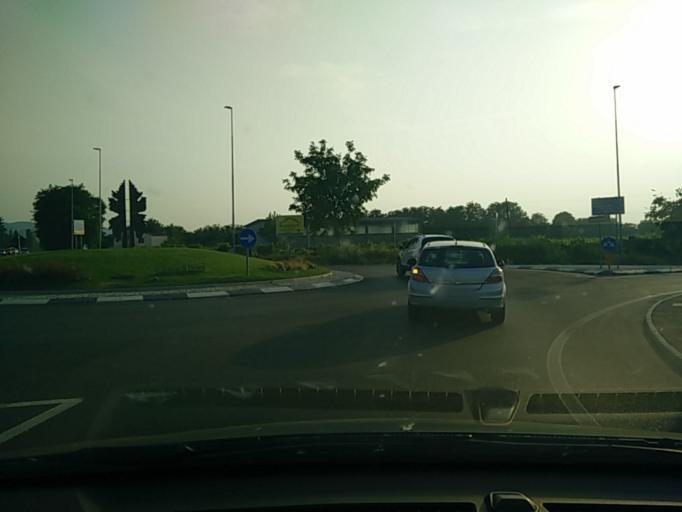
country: IT
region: Lombardy
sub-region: Provincia di Pavia
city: Broni
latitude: 45.0578
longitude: 9.2491
